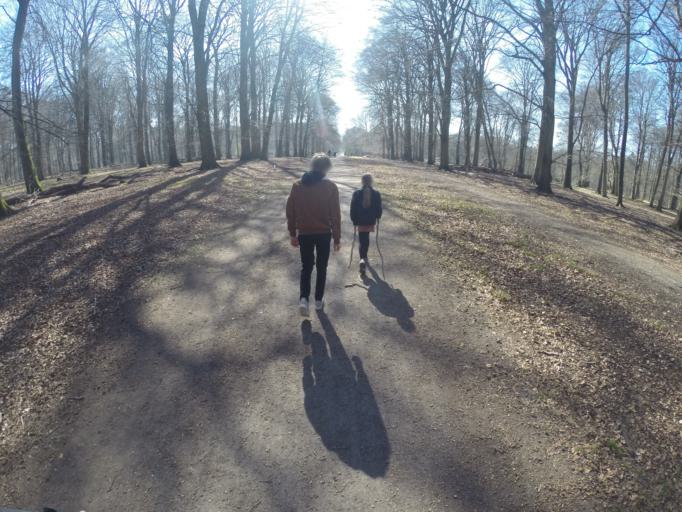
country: DK
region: Capital Region
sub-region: Gentofte Kommune
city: Charlottenlund
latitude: 55.7821
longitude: 12.5541
